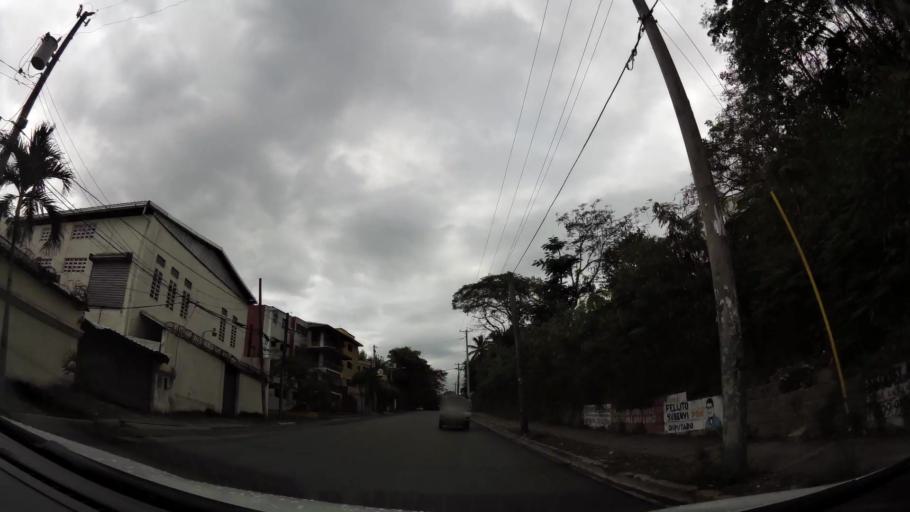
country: DO
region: Nacional
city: La Agustina
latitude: 18.5051
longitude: -69.9339
